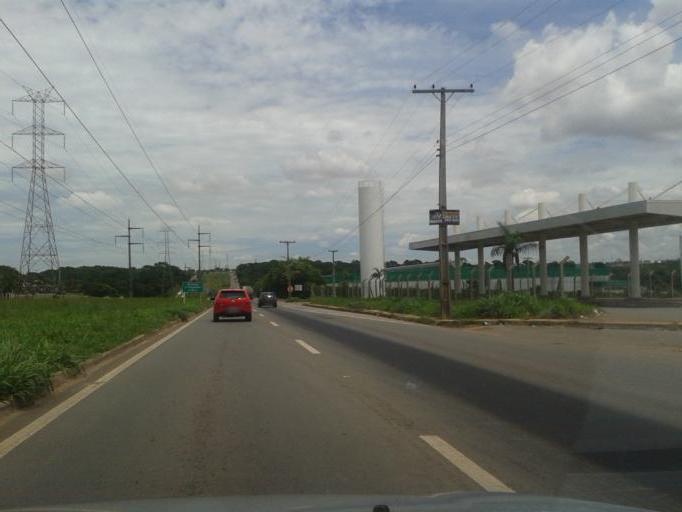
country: BR
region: Goias
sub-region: Aparecida De Goiania
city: Aparecida de Goiania
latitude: -16.7860
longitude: -49.2532
